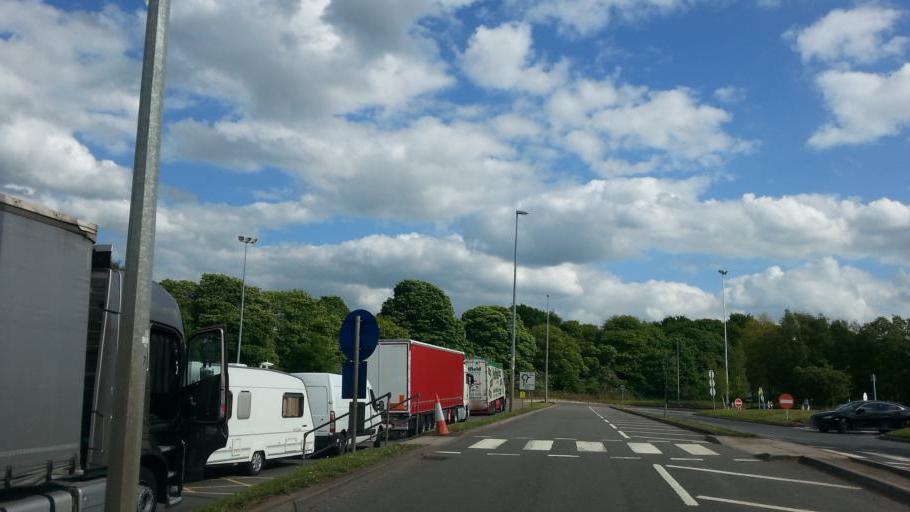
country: GB
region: England
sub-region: Nottinghamshire
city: Bircotes
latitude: 53.3880
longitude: -1.0600
